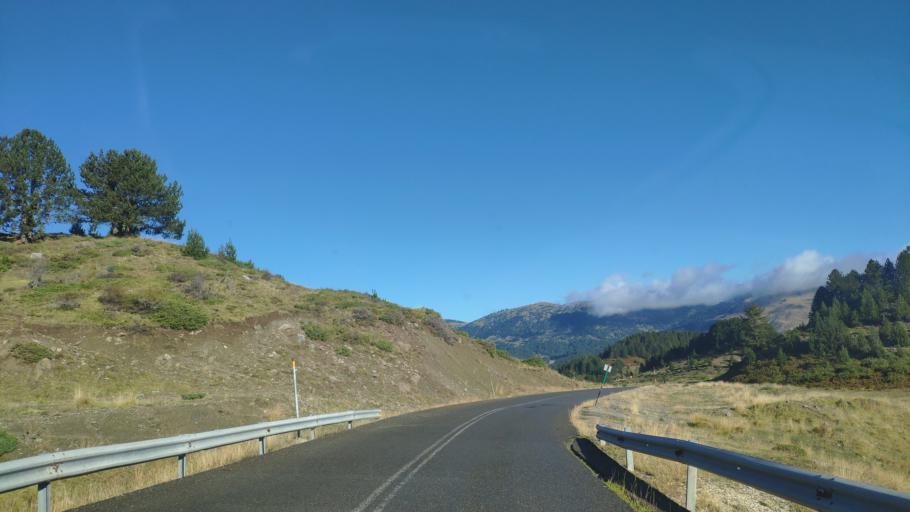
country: GR
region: Epirus
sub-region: Nomos Ioanninon
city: Metsovo
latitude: 39.8007
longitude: 21.1750
